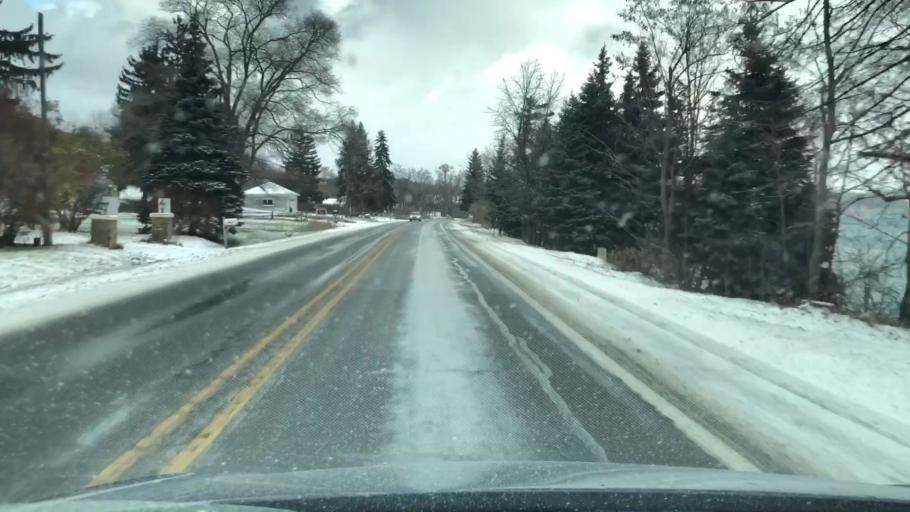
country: US
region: Michigan
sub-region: Grand Traverse County
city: Traverse City
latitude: 44.8147
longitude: -85.5582
